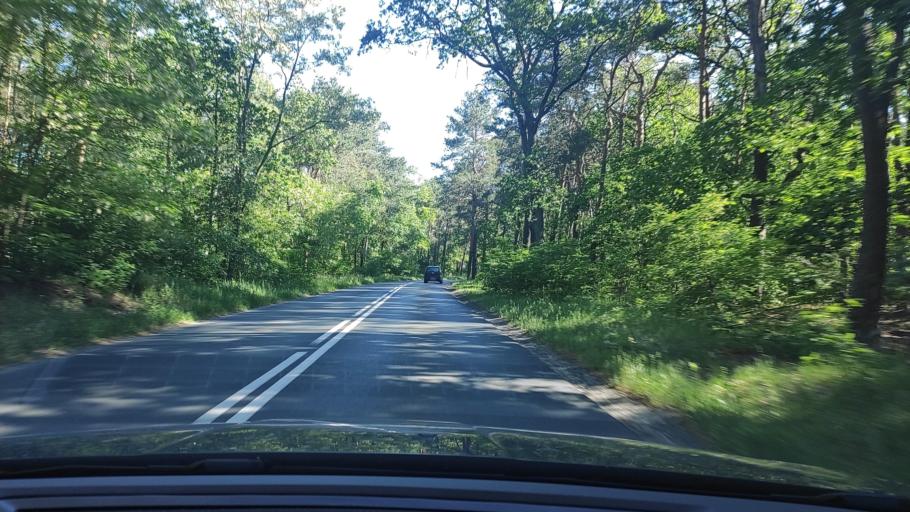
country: PL
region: Greater Poland Voivodeship
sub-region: Powiat poznanski
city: Swarzedz
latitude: 52.3929
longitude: 17.0357
